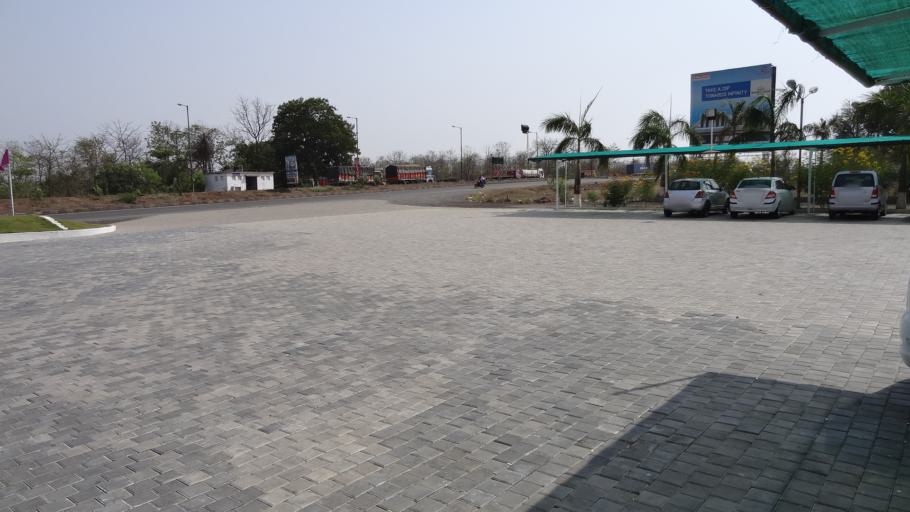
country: IN
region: Maharashtra
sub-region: Thane
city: Vasind
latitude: 19.3956
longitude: 73.2364
